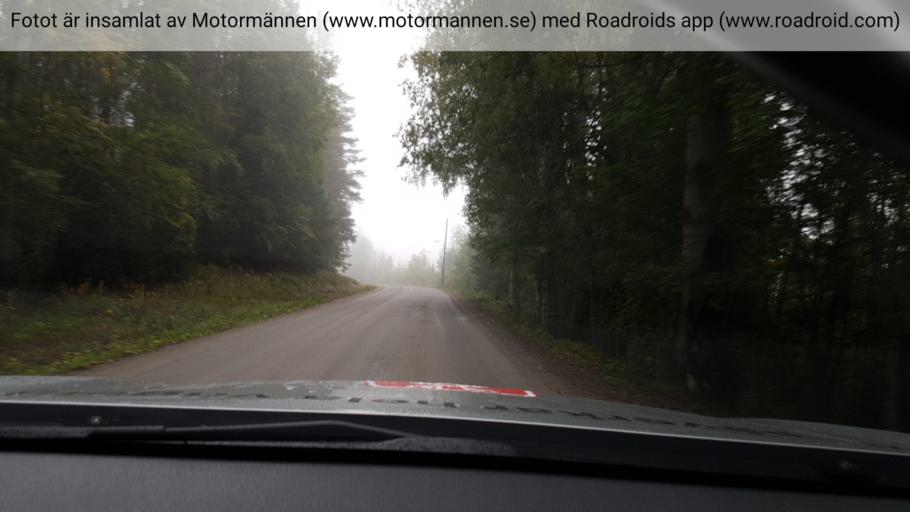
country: SE
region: Vaesterbotten
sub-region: Vannas Kommun
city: Vannasby
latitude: 64.0866
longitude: 20.0456
